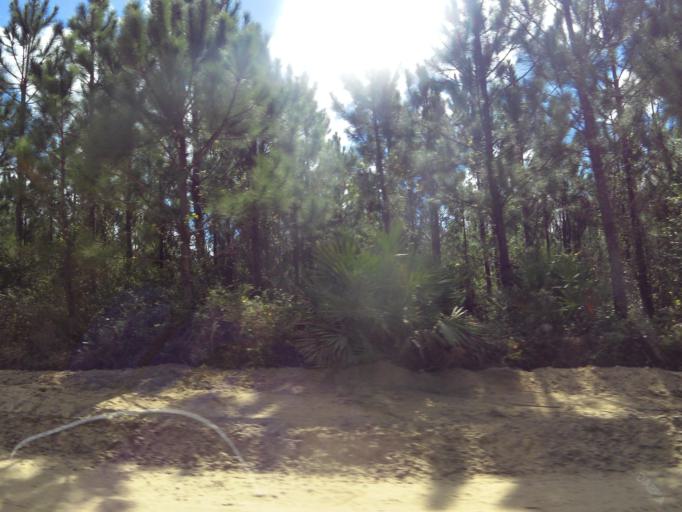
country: US
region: Florida
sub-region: Clay County
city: Keystone Heights
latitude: 29.8153
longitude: -81.8381
